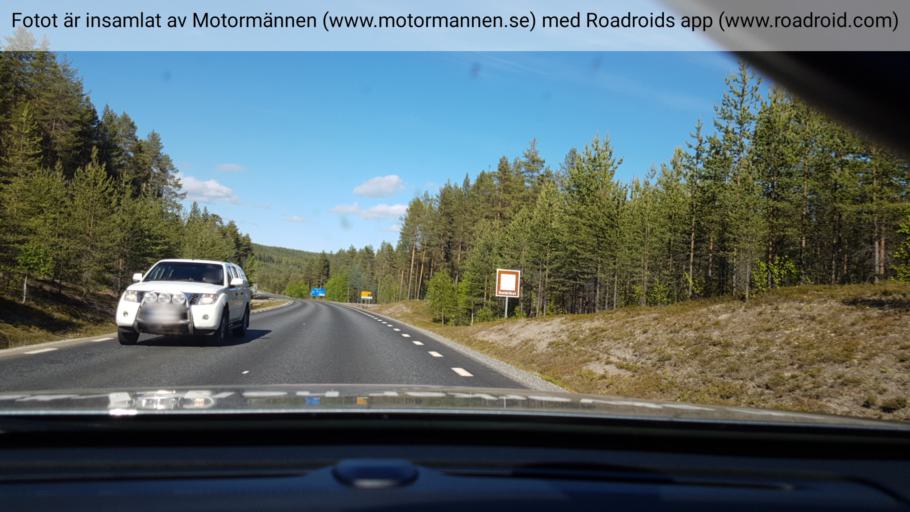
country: SE
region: Vaesterbotten
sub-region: Lycksele Kommun
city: Lycksele
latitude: 64.8201
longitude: 18.7868
